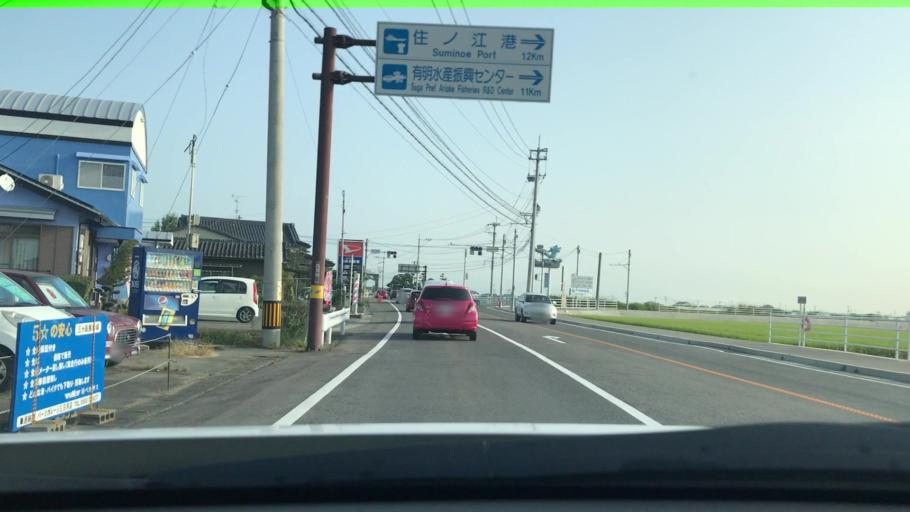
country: JP
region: Saga Prefecture
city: Saga-shi
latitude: 33.2028
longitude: 130.2046
